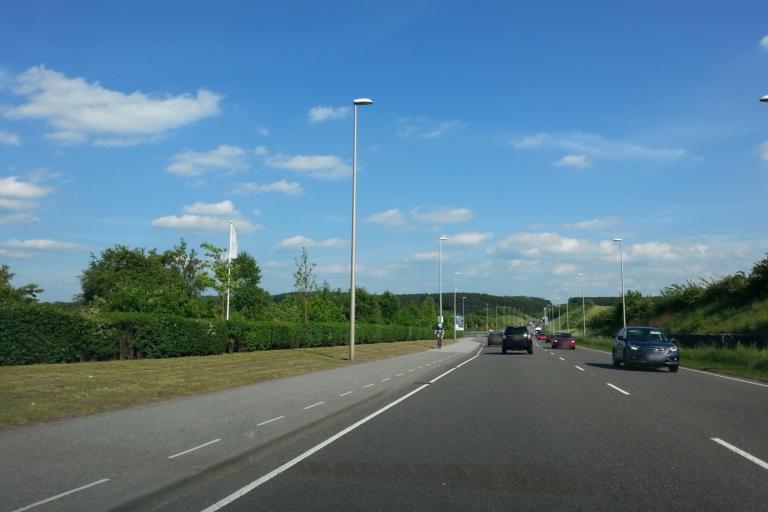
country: GB
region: England
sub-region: Nottinghamshire
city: Mansfield
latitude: 53.1252
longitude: -1.2190
